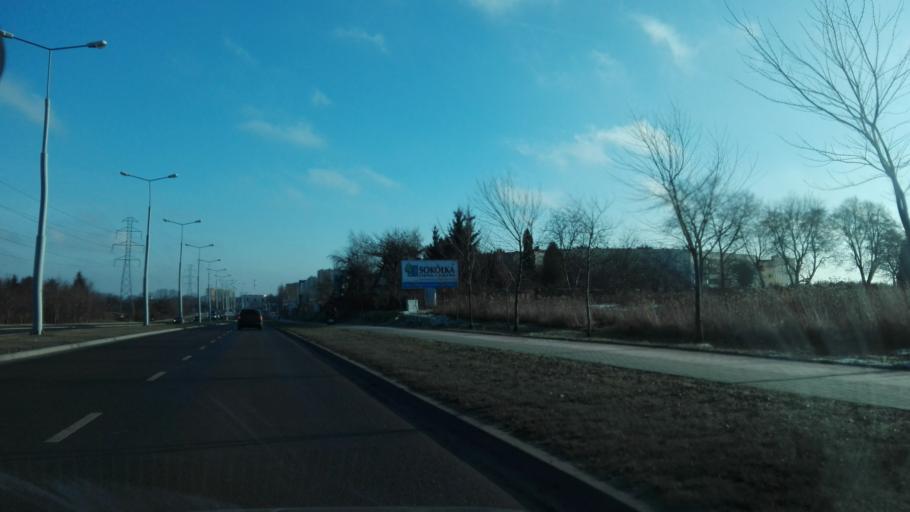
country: PL
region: Lublin Voivodeship
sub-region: Powiat lubelski
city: Kozubszczyzna
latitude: 51.2266
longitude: 22.4860
